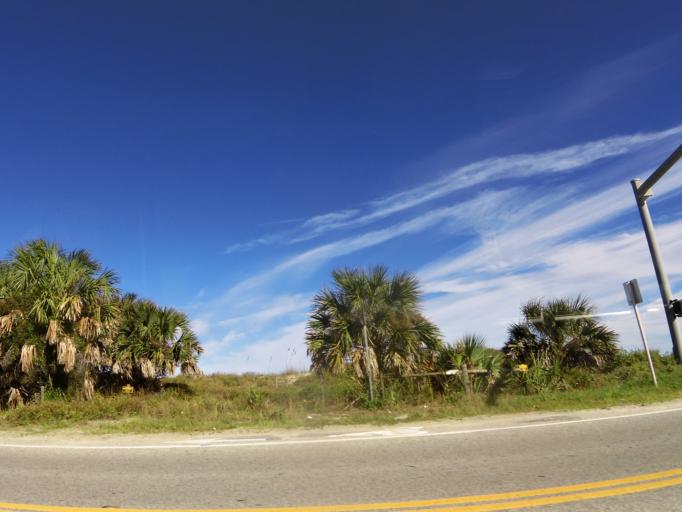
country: US
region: Florida
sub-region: Saint Johns County
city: Saint Augustine Beach
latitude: 29.8596
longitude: -81.2672
